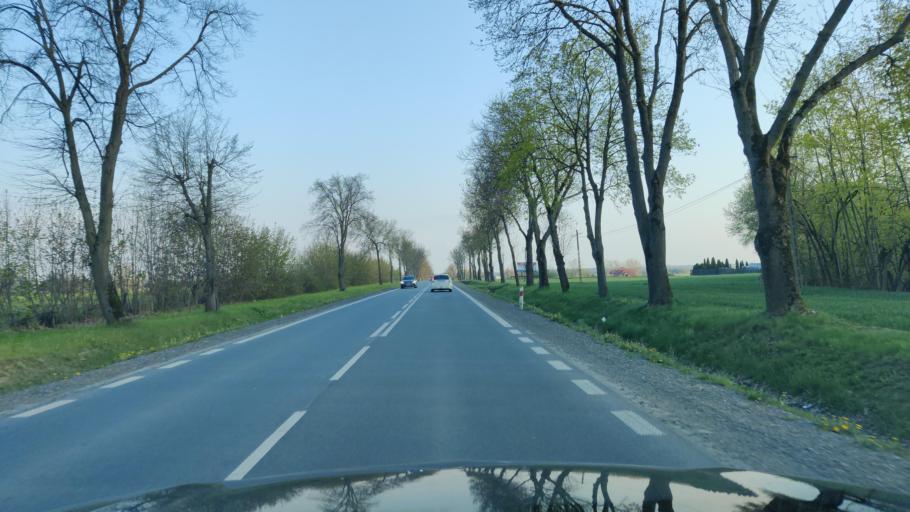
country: PL
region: Masovian Voivodeship
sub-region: Powiat pultuski
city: Pultusk
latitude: 52.6819
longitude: 21.0808
